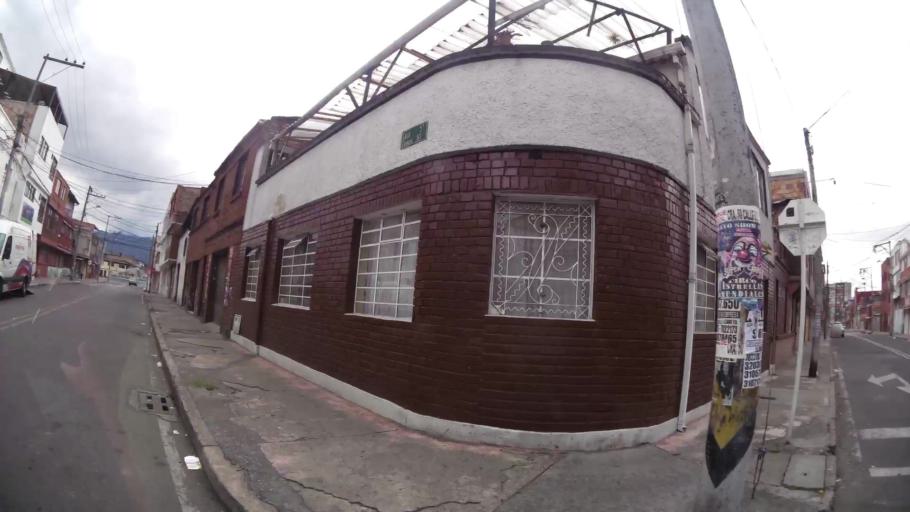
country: CO
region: Bogota D.C.
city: Bogota
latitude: 4.6263
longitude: -74.1185
